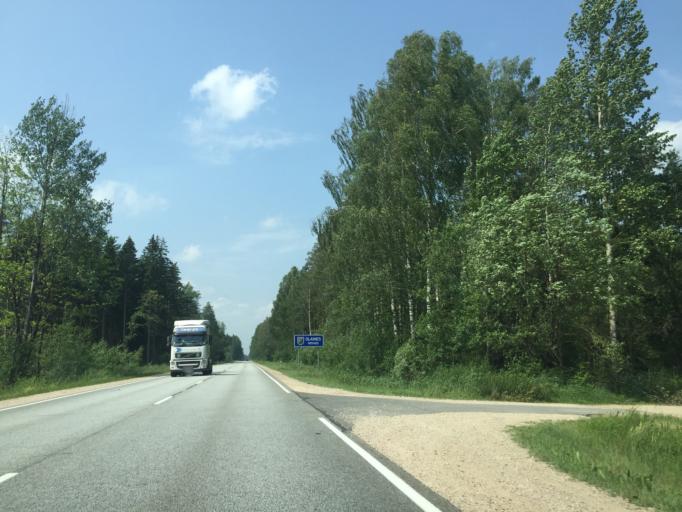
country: LV
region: Kekava
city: Balozi
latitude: 56.8148
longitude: 24.1384
